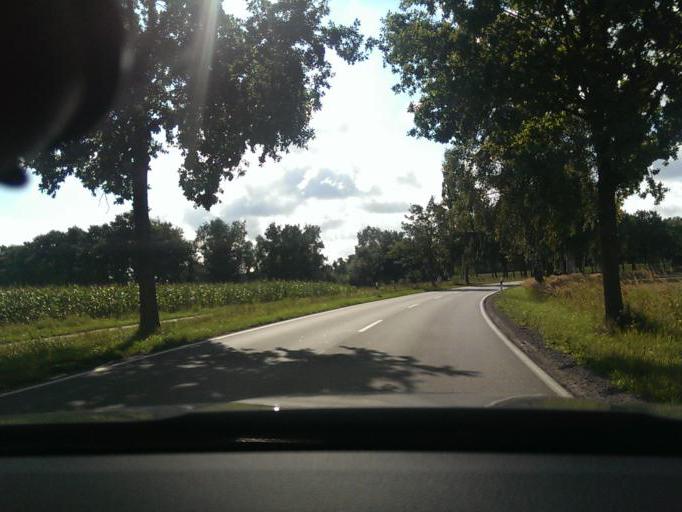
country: DE
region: Lower Saxony
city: Isernhagen Farster Bauerschaft
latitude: 52.4460
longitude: 9.8458
